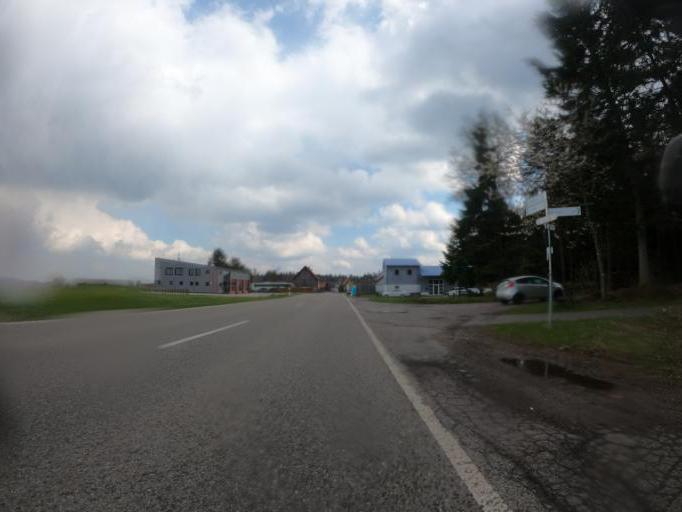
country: DE
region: Baden-Wuerttemberg
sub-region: Karlsruhe Region
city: Oberreichenbach
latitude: 48.7440
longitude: 8.6586
